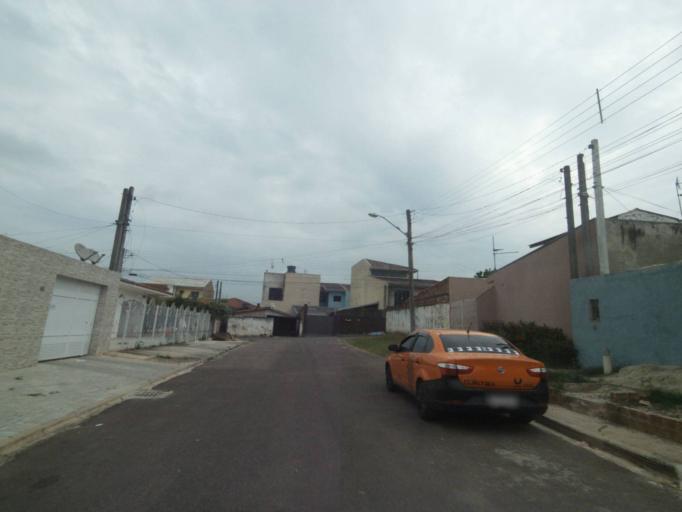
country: BR
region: Parana
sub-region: Sao Jose Dos Pinhais
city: Sao Jose dos Pinhais
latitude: -25.5498
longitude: -49.2648
